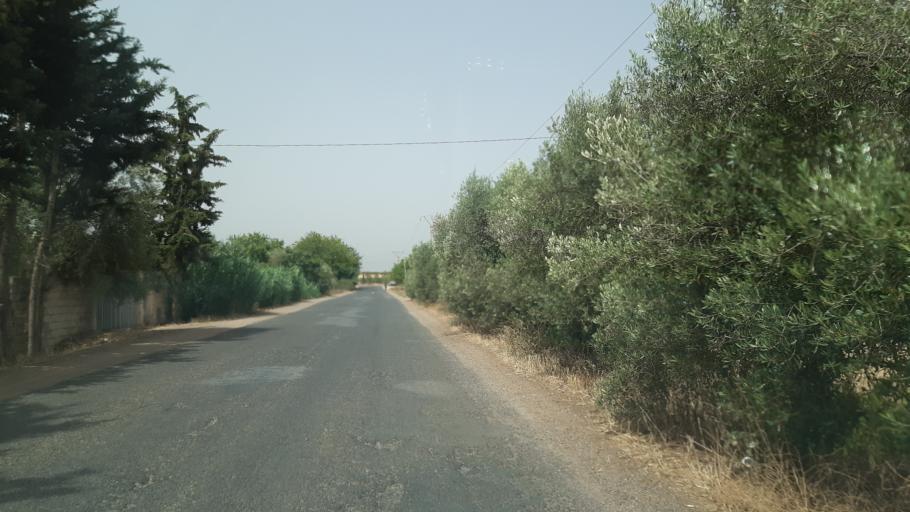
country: MA
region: Fes-Boulemane
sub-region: Fes
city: Oulad Tayeb
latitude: 33.8459
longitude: -5.1113
